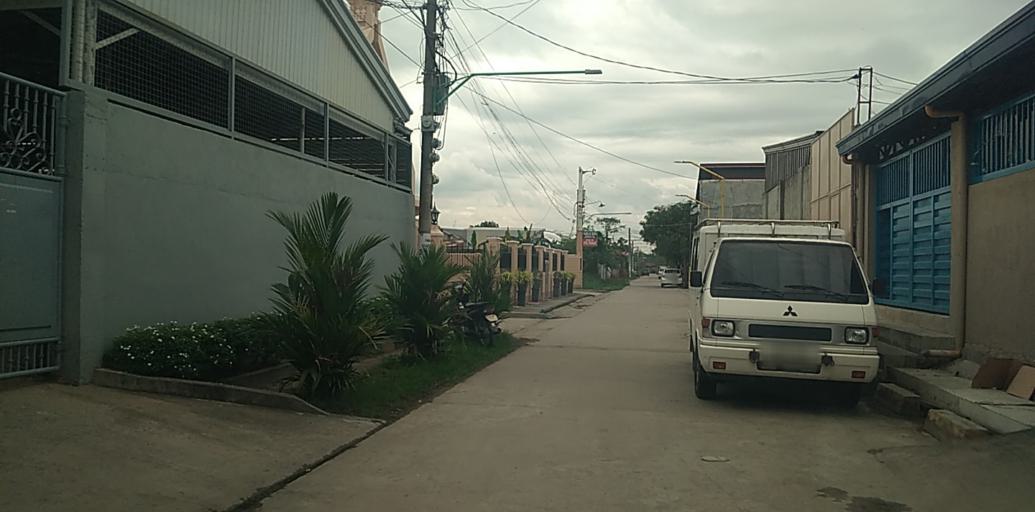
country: PH
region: Central Luzon
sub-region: Province of Pampanga
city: San Fernando
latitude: 14.9998
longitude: 120.7032
